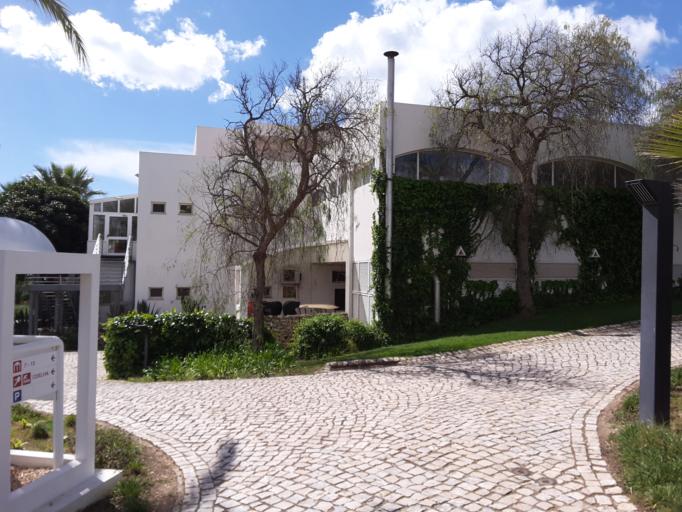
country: PT
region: Faro
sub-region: Albufeira
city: Albufeira
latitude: 37.0763
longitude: -8.2961
